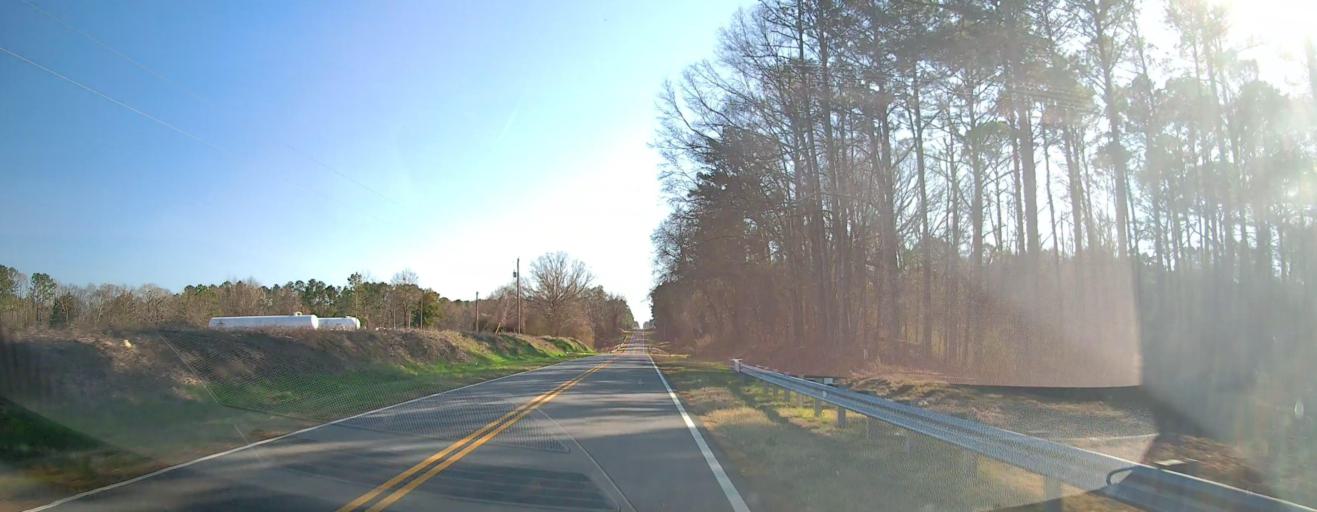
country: US
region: Georgia
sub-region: Sumter County
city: Americus
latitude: 32.0792
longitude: -84.1662
